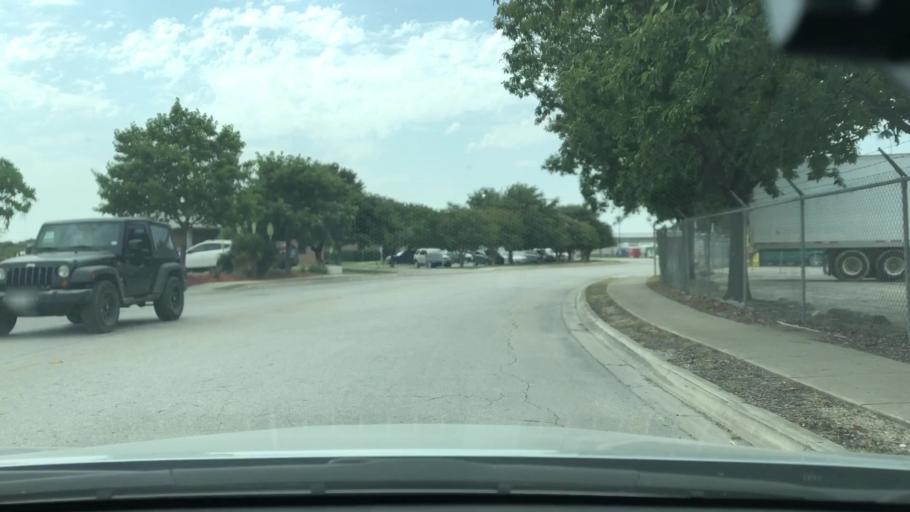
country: US
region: Texas
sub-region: Bexar County
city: Kirby
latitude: 29.4605
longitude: -98.4020
